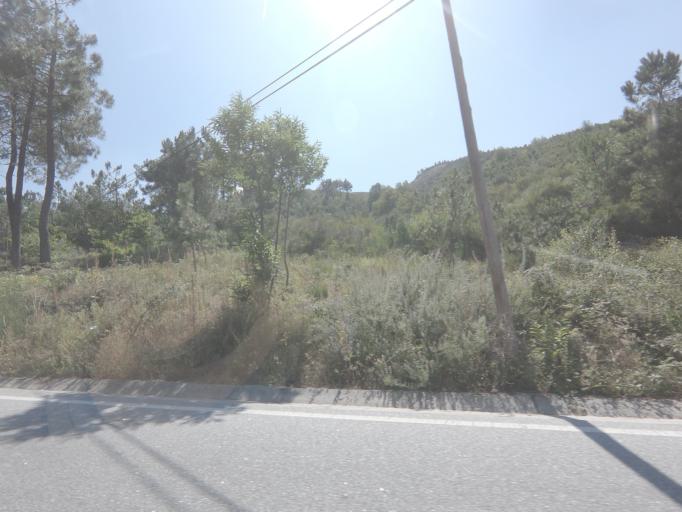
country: PT
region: Viseu
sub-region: Tarouca
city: Tarouca
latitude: 41.0032
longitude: -7.7819
